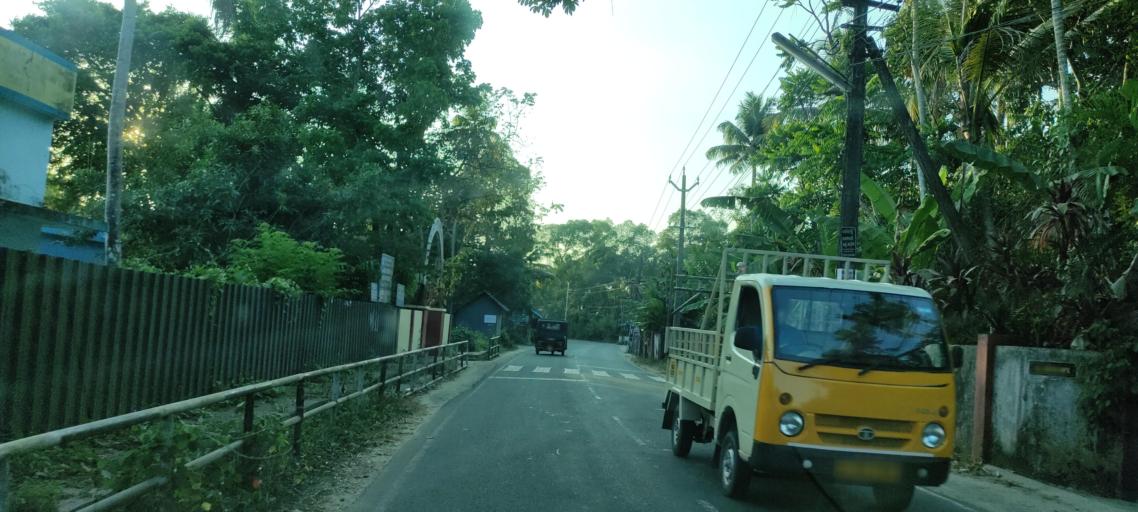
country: IN
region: Kerala
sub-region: Alappuzha
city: Kutiatodu
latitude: 9.7731
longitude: 76.3488
